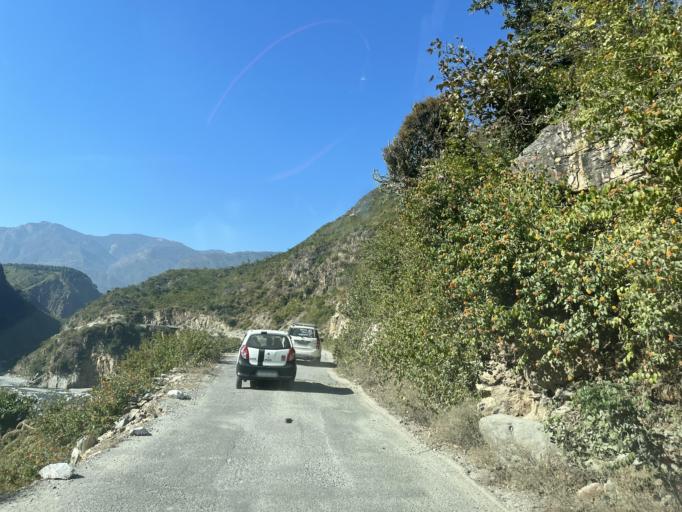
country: IN
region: Uttarakhand
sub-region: Naini Tal
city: Naini Tal
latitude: 29.5109
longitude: 79.4697
